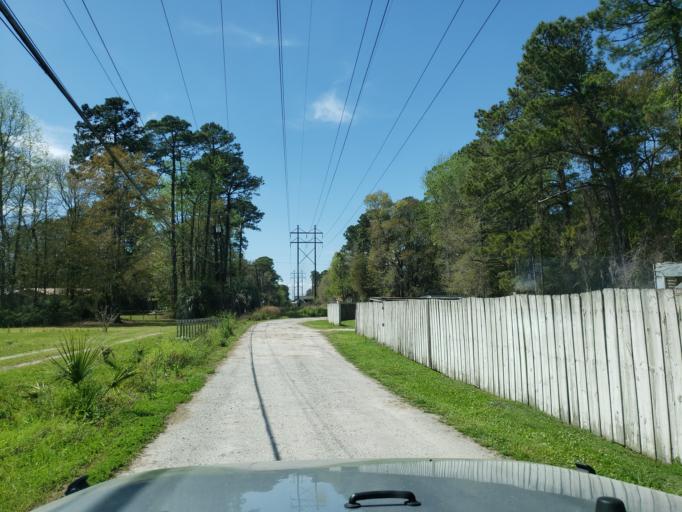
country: US
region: Georgia
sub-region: Chatham County
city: Montgomery
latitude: 31.9525
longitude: -81.1153
